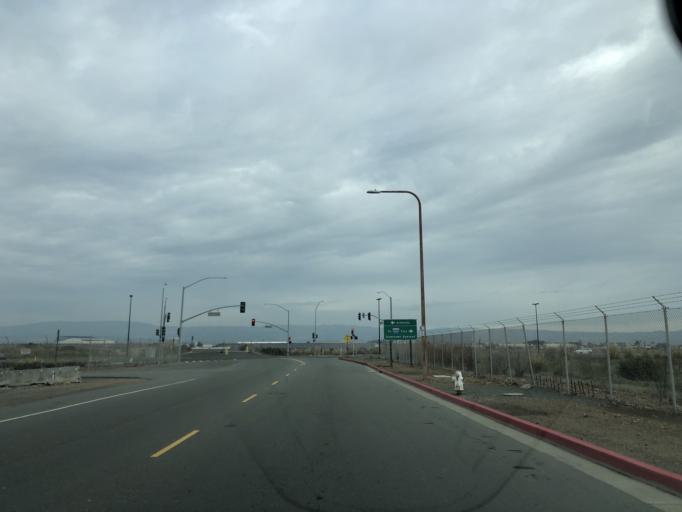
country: US
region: California
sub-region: Alameda County
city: Alameda
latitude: 37.7224
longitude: -122.2179
